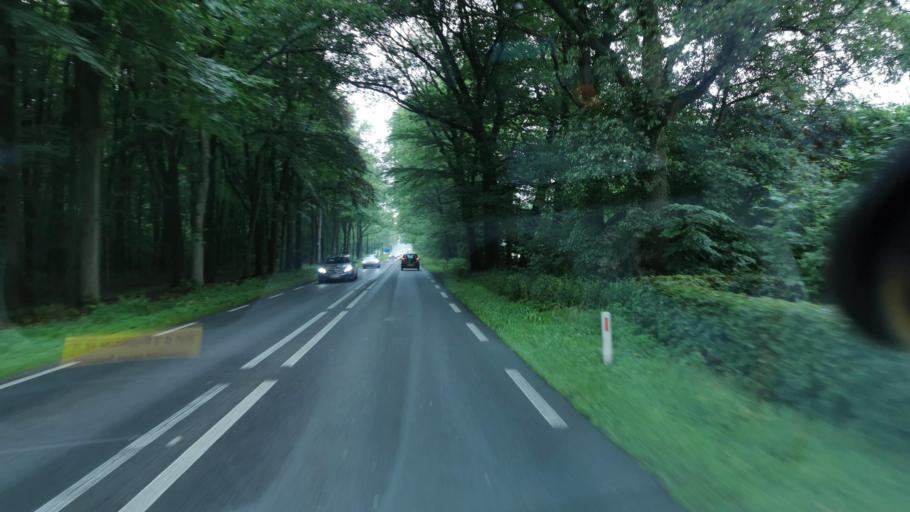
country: NL
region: Overijssel
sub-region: Gemeente Losser
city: Losser
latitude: 52.2765
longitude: 6.9756
